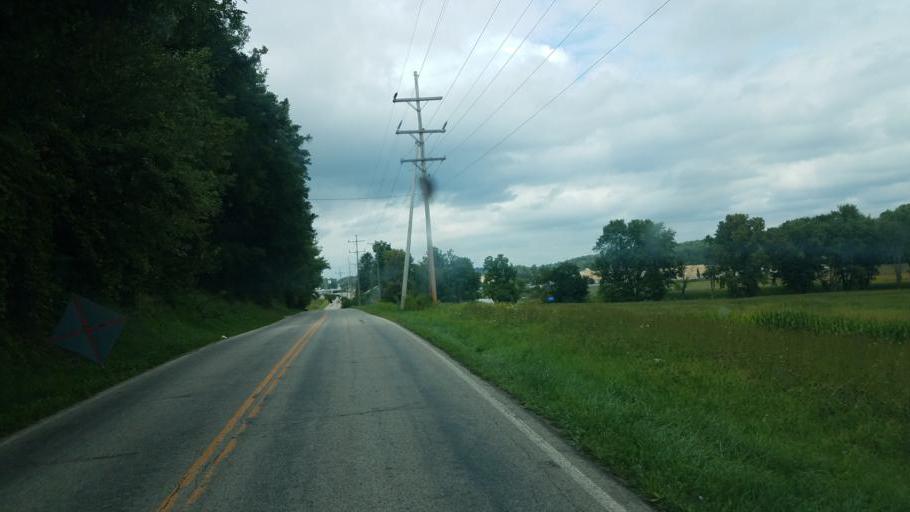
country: US
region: Ohio
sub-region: Sandusky County
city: Bellville
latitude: 40.6863
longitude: -82.5113
